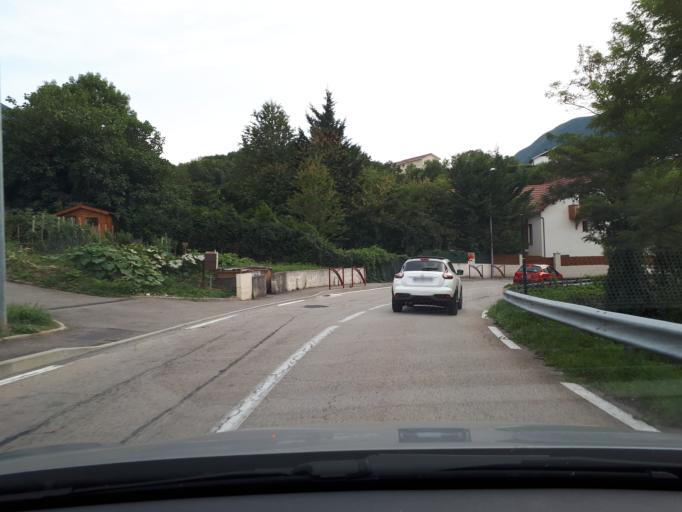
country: FR
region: Rhone-Alpes
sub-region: Departement de l'Isere
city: Saint-Georges-de-Commiers
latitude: 45.0431
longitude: 5.7043
